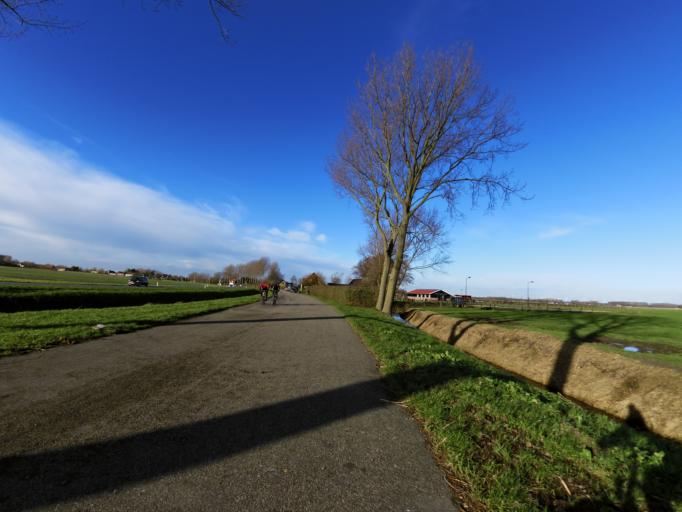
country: NL
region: South Holland
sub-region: Gemeente Hellevoetsluis
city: Nieuw-Helvoet
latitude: 51.8747
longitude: 4.0912
